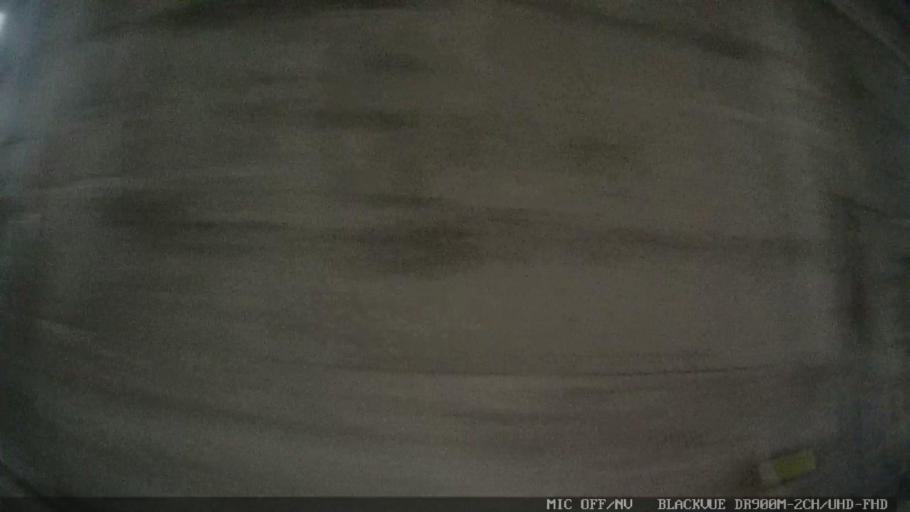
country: BR
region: Sao Paulo
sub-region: Cubatao
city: Cubatao
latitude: -23.8934
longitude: -46.5066
